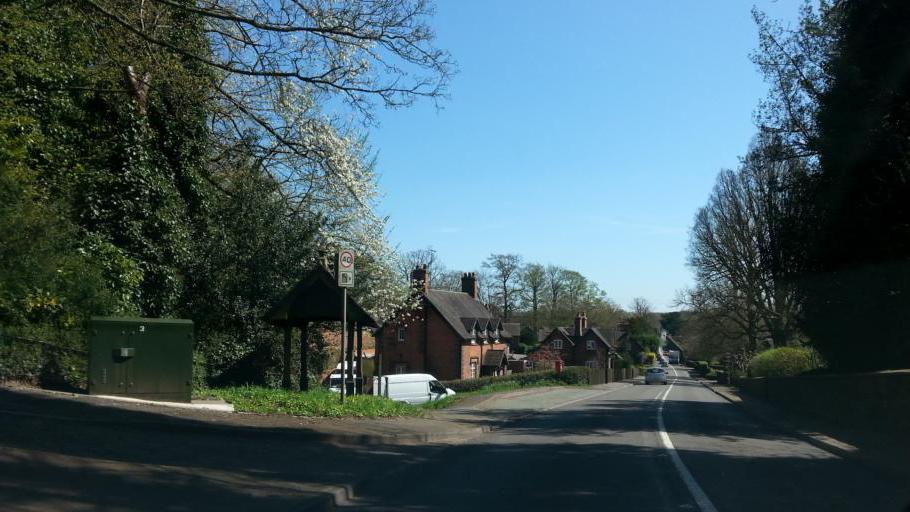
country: GB
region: England
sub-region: Shropshire
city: Tong
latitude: 52.6955
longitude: -2.2922
